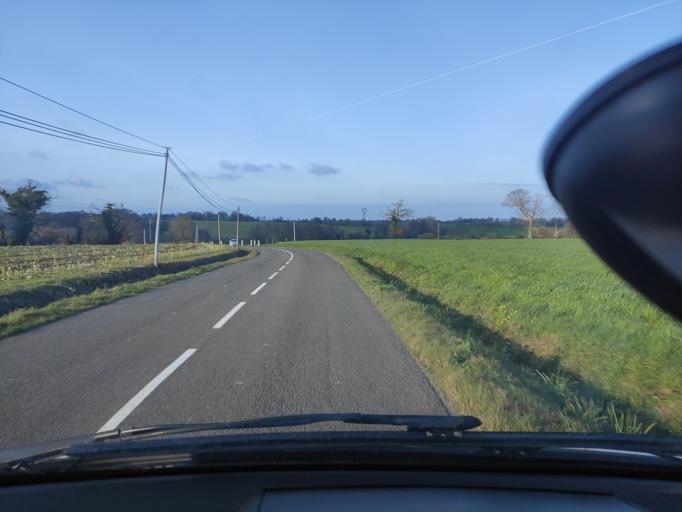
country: FR
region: Pays de la Loire
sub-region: Departement de la Vendee
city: La Chaize-le-Vicomte
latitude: 46.6503
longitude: -1.2968
